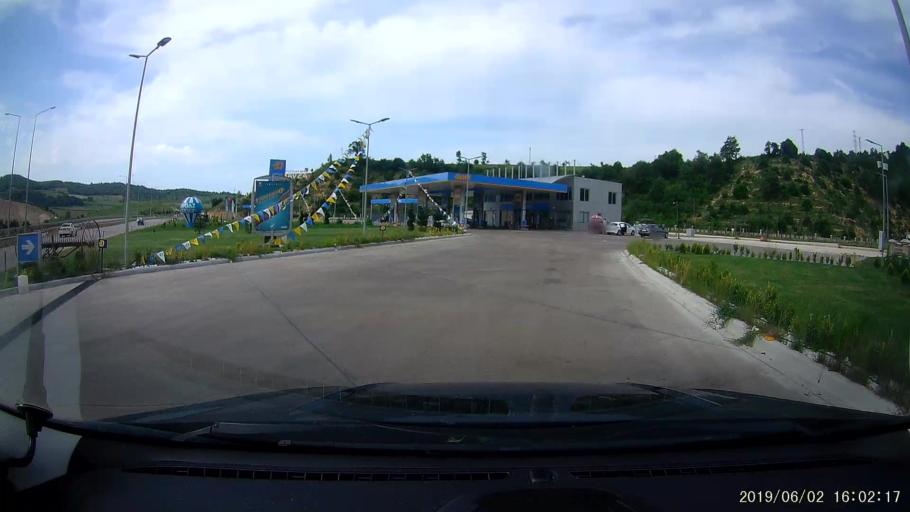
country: TR
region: Samsun
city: Havza
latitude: 40.9415
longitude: 35.6586
